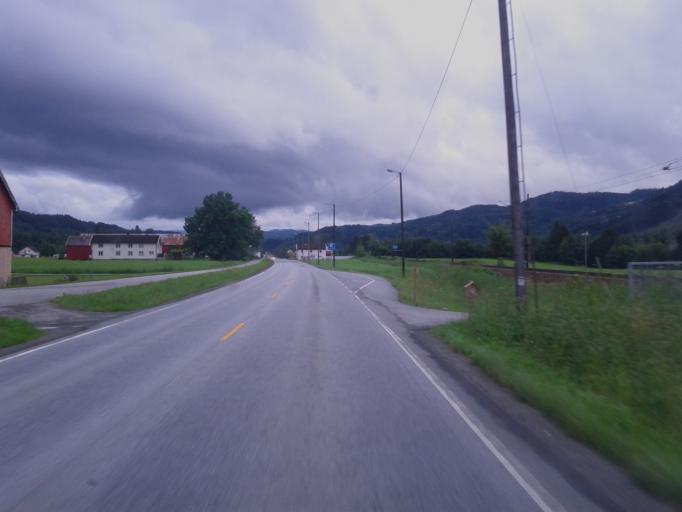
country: NO
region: Sor-Trondelag
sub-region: Melhus
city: Lundamo
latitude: 63.1470
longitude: 10.2677
